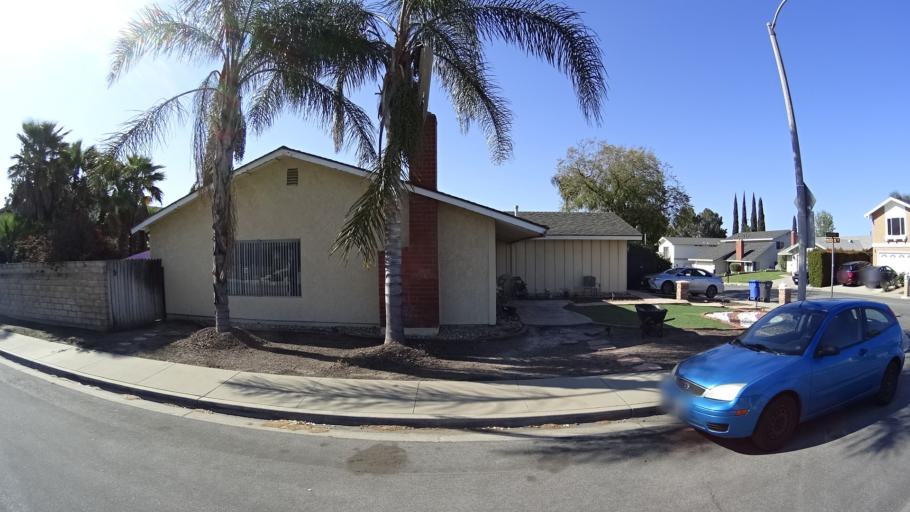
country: US
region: California
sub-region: Ventura County
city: Thousand Oaks
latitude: 34.2112
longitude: -118.8351
